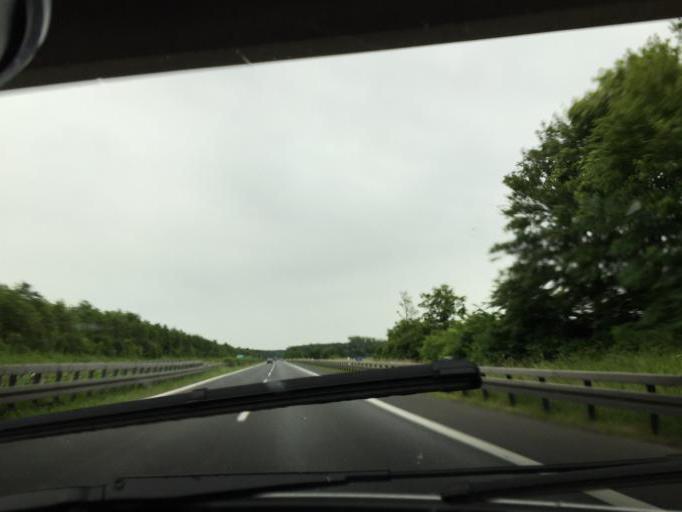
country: DE
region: Bavaria
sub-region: Regierungsbezirk Unterfranken
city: Wonfurt
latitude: 50.0044
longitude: 10.4625
